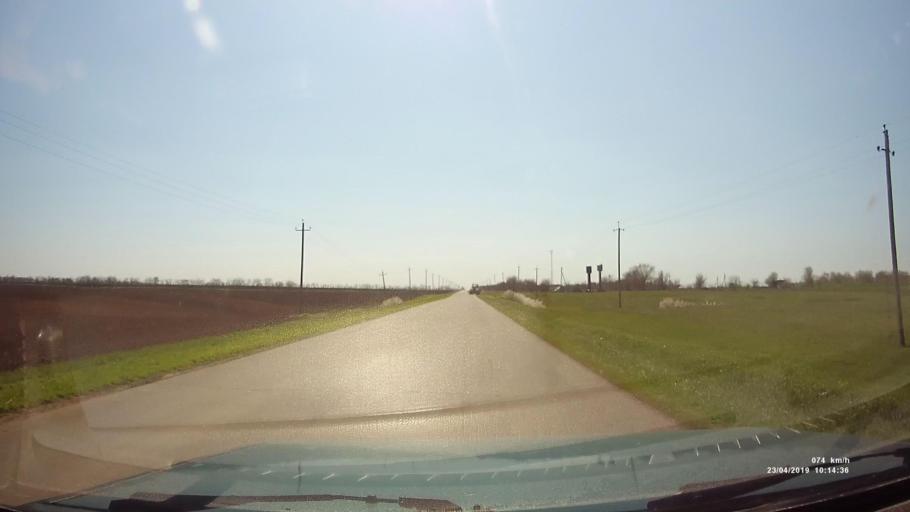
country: RU
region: Rostov
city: Sovetskoye
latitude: 46.6752
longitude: 42.3716
